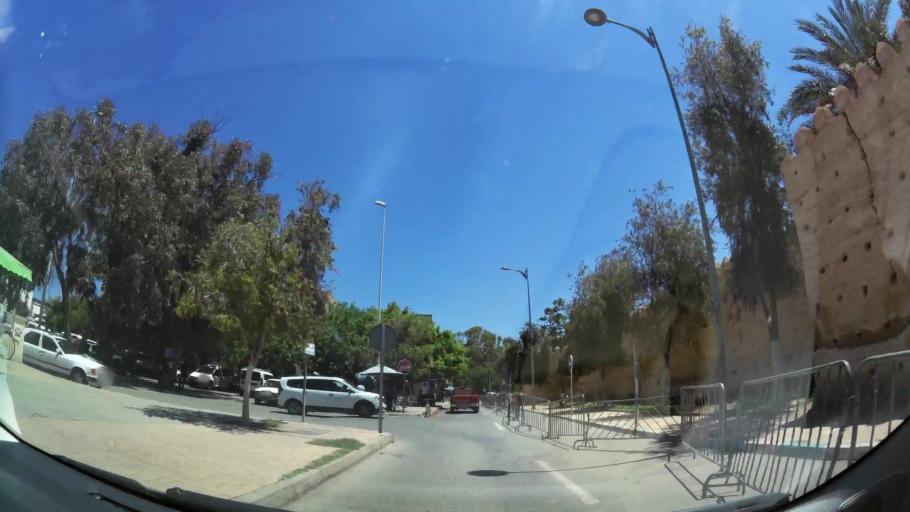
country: MA
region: Oriental
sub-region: Berkane-Taourirt
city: Madagh
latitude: 35.0804
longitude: -2.2147
